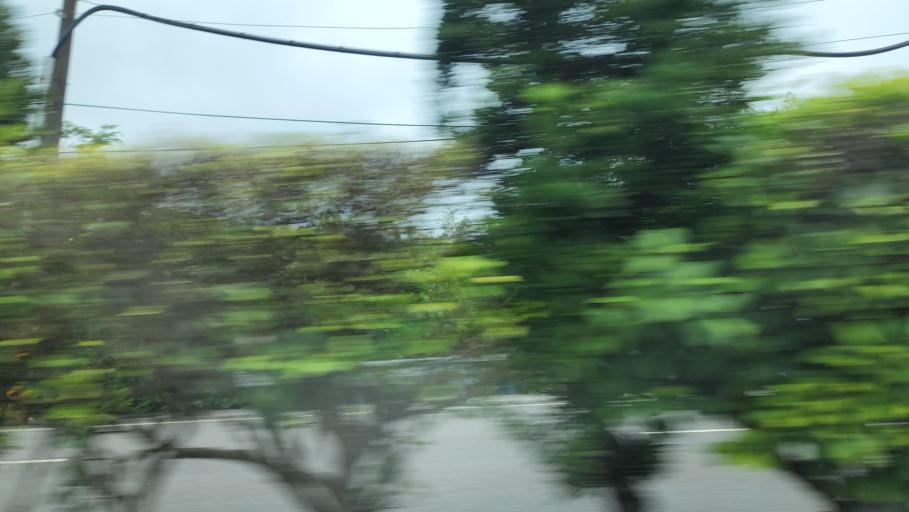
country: TW
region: Taiwan
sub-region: Keelung
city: Keelung
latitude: 25.2118
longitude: 121.6472
